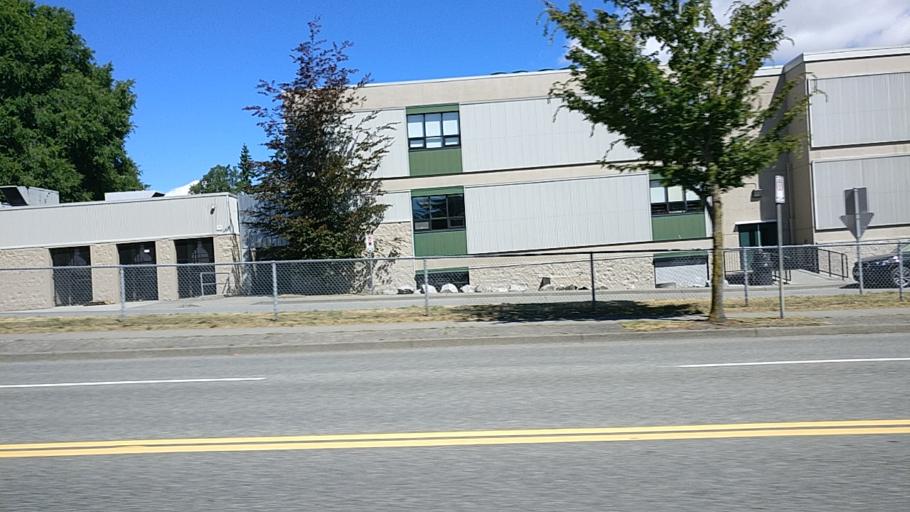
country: CA
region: British Columbia
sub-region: Greater Vancouver Regional District
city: White Rock
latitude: 49.0310
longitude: -122.7859
